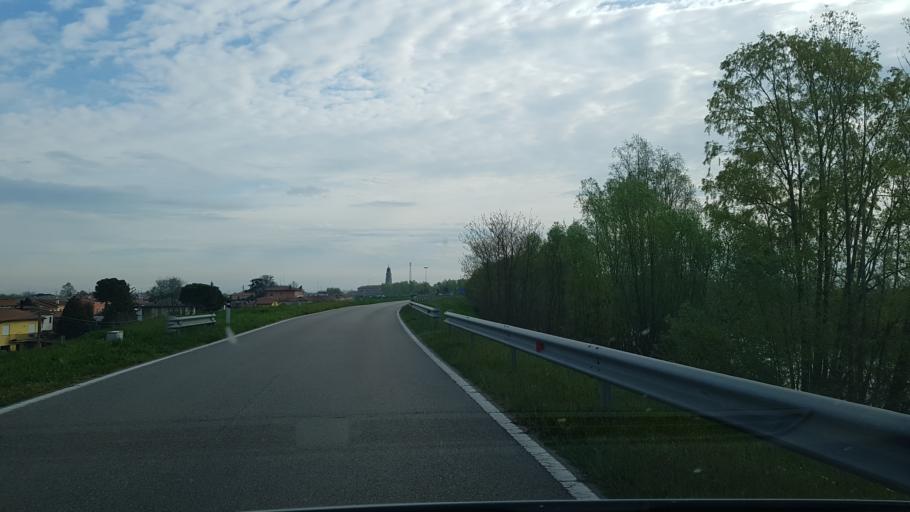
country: IT
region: Veneto
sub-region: Provincia di Padova
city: Boara Pisani
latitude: 45.1038
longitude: 11.7796
